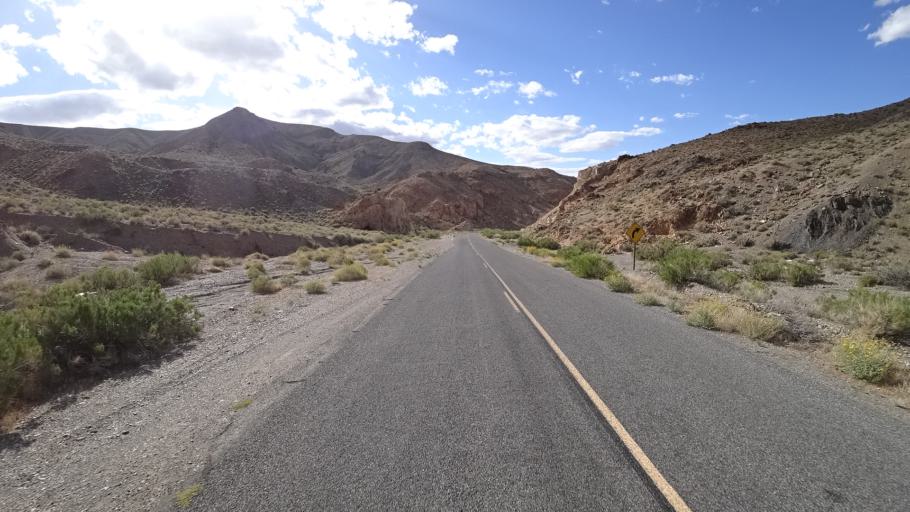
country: US
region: Nevada
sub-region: Nye County
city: Beatty
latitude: 36.4241
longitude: -117.1911
